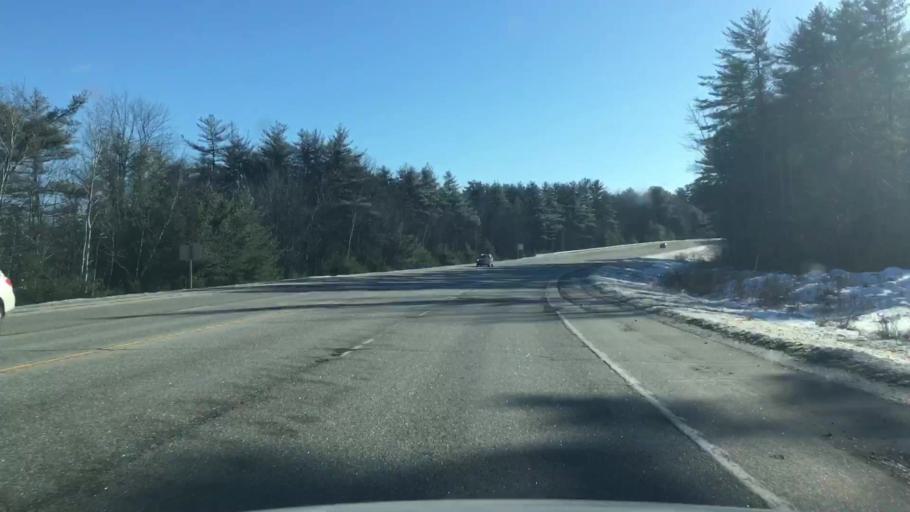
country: US
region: Maine
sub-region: Androscoggin County
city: Turner
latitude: 44.1799
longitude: -70.2324
